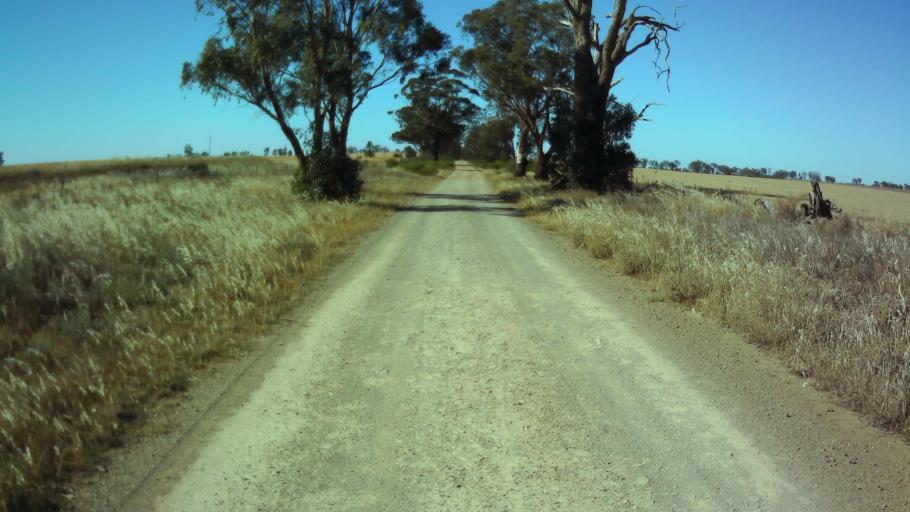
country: AU
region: New South Wales
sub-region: Weddin
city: Grenfell
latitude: -33.8868
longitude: 147.8812
